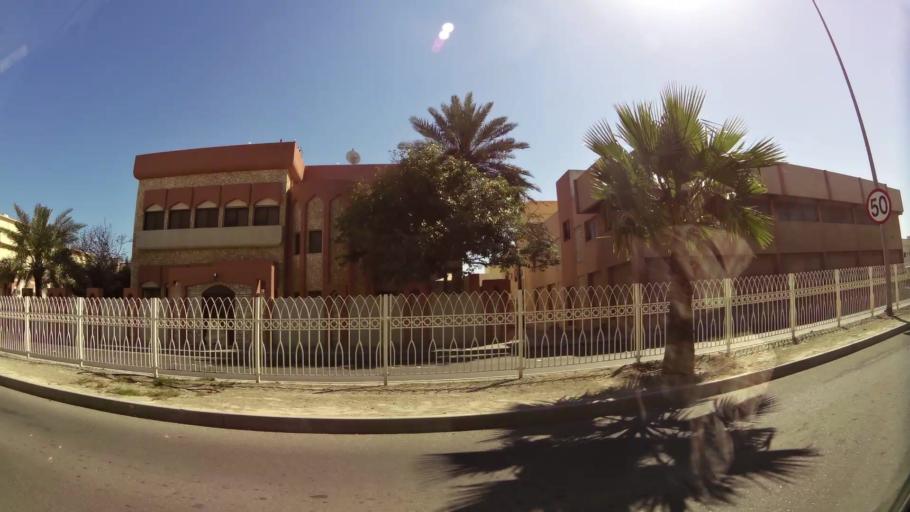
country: BH
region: Muharraq
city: Al Muharraq
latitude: 26.2575
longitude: 50.6078
